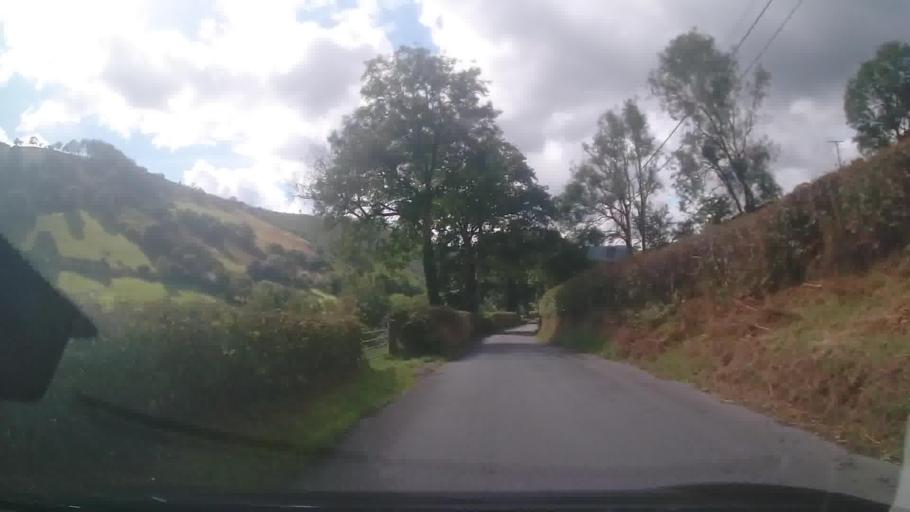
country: GB
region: Wales
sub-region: Gwynedd
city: Bala
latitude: 52.7328
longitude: -3.6554
